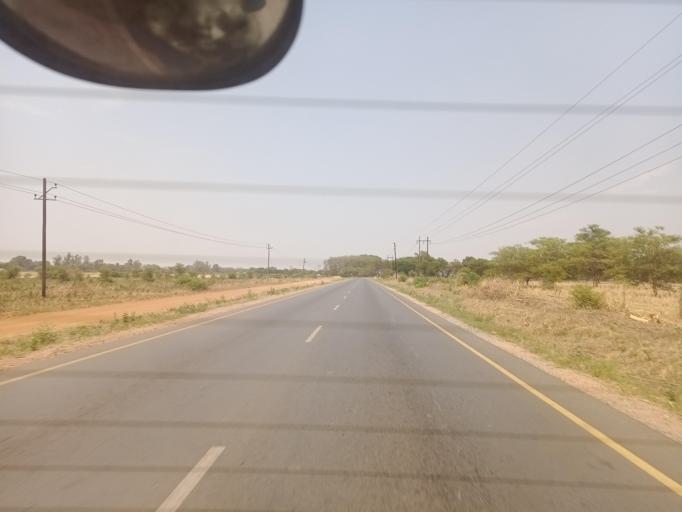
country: ZM
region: Lusaka
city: Lusaka
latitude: -15.2714
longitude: 28.4100
